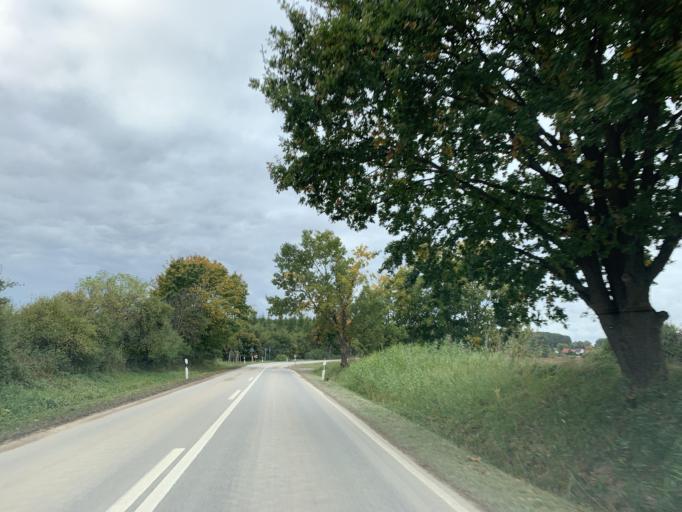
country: DE
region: Mecklenburg-Vorpommern
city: Blankensee
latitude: 53.3953
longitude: 13.2789
